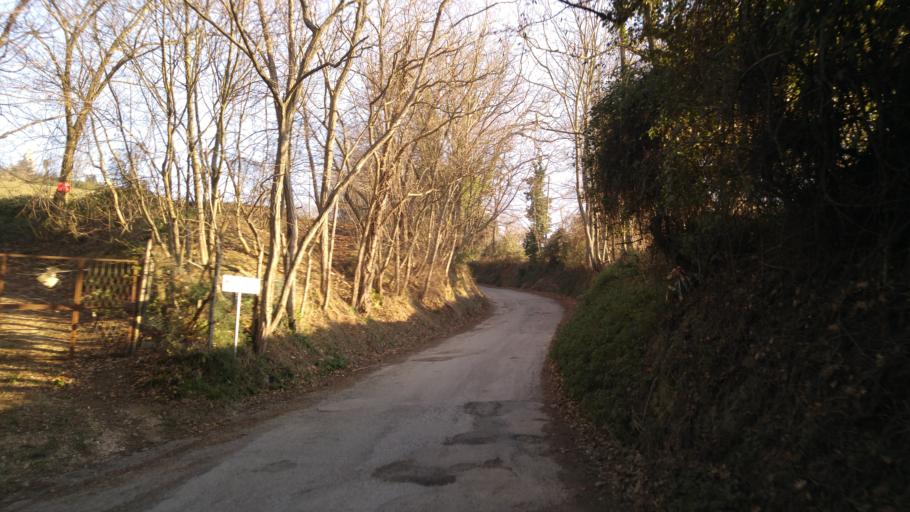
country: IT
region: The Marches
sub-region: Provincia di Pesaro e Urbino
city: Fenile
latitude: 43.8640
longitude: 12.9497
